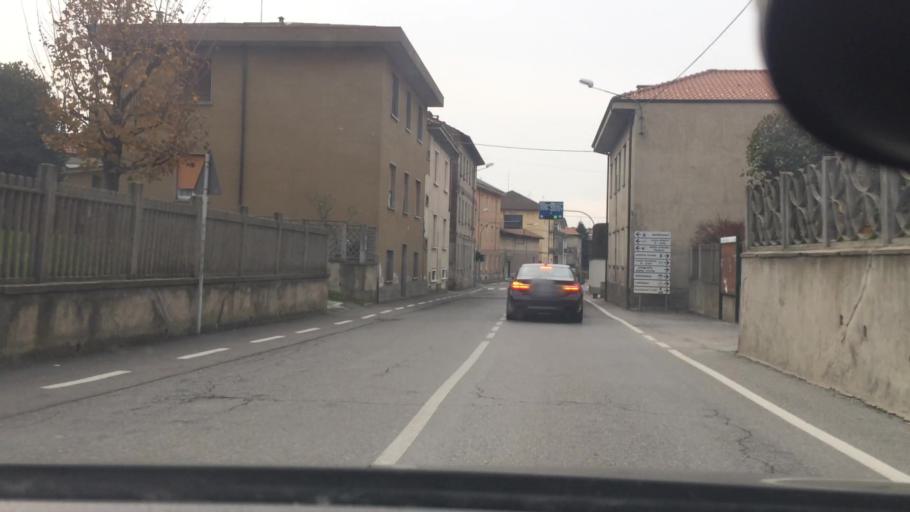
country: IT
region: Lombardy
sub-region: Provincia di Monza e Brianza
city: Cogliate
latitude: 45.6461
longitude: 9.0802
